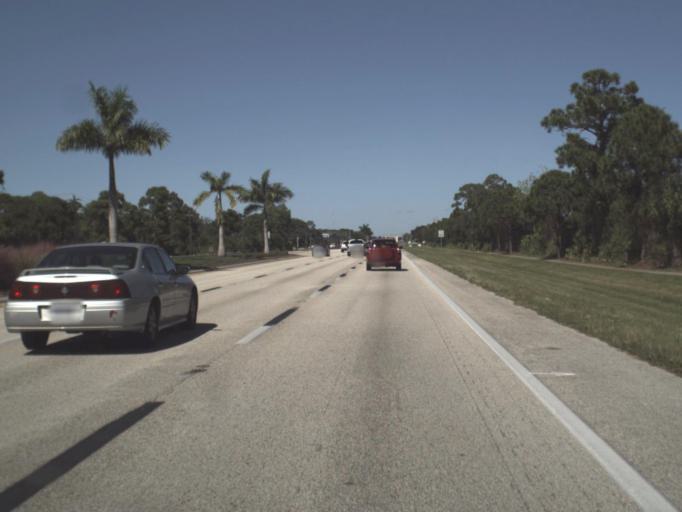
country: US
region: Florida
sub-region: Lee County
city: San Carlos Park
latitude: 26.4689
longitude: -81.8342
